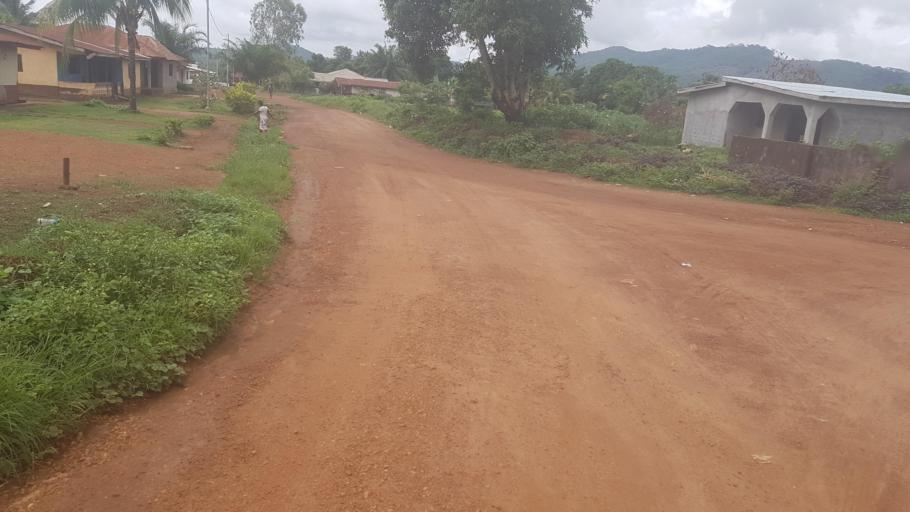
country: SL
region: Southern Province
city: Mogbwemo
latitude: 7.7602
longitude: -12.3061
